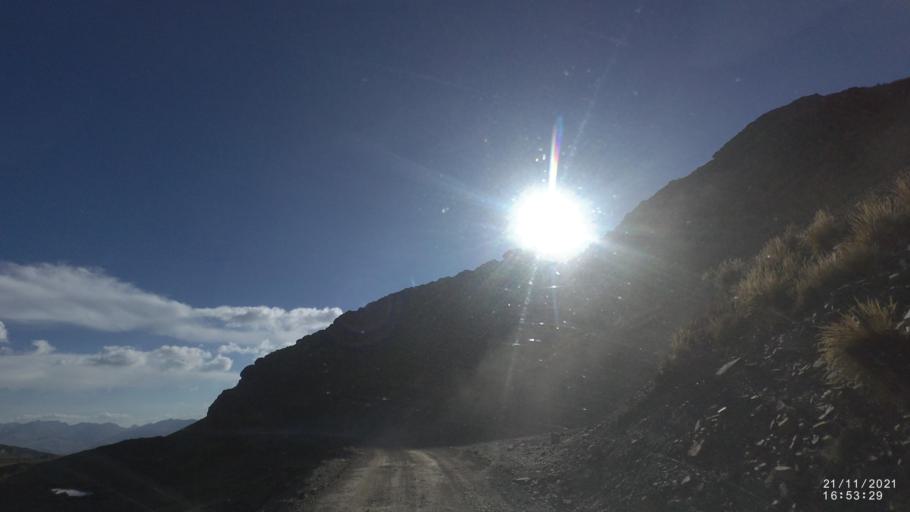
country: BO
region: Cochabamba
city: Cochabamba
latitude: -17.0861
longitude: -66.2533
